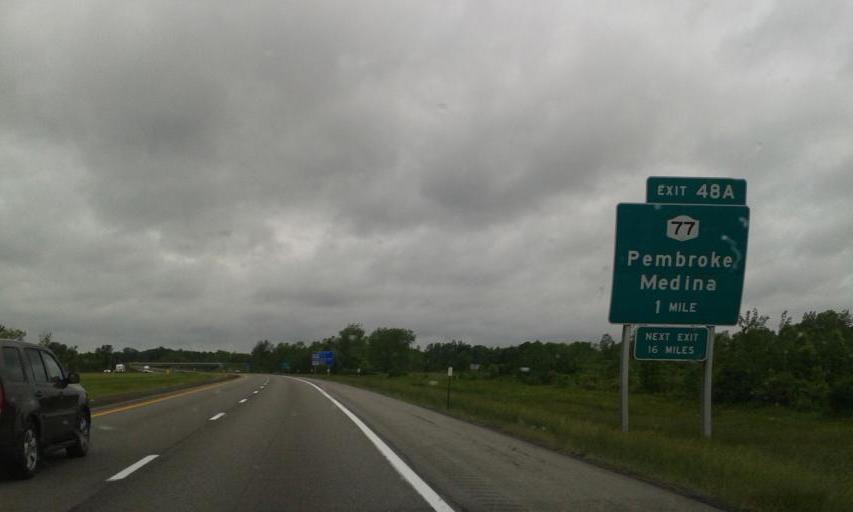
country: US
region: New York
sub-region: Erie County
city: Akron
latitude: 43.0098
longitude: -78.3967
